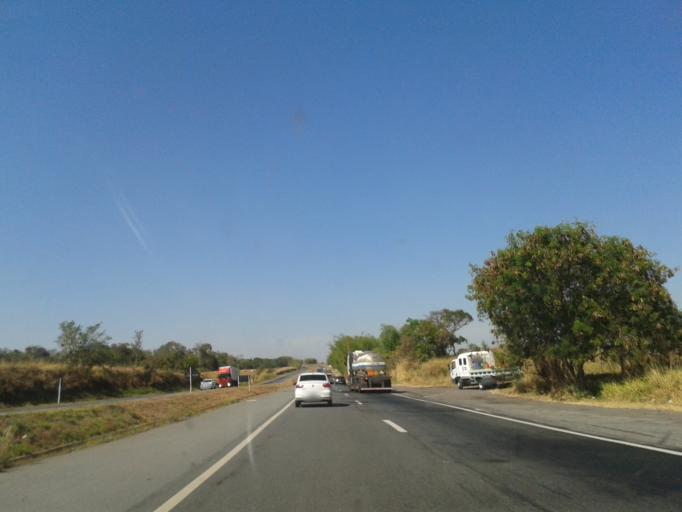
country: BR
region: Goias
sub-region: Piracanjuba
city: Piracanjuba
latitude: -17.2628
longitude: -49.2412
